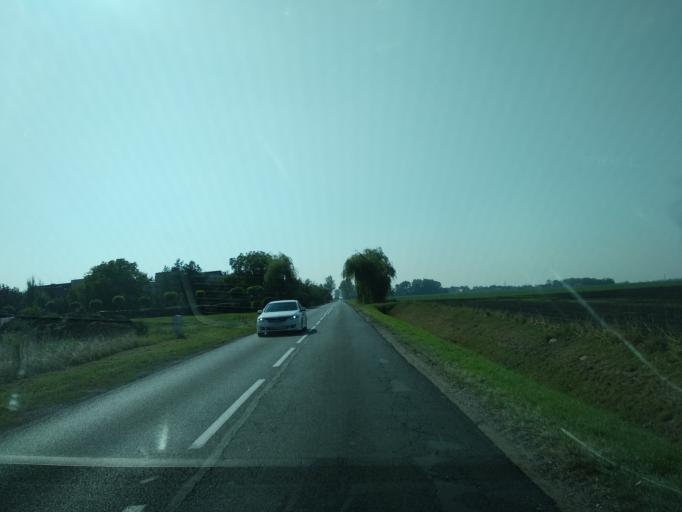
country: PL
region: Lower Silesian Voivodeship
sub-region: Powiat wroclawski
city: Zerniki Wroclawskie
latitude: 51.0348
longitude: 17.0307
